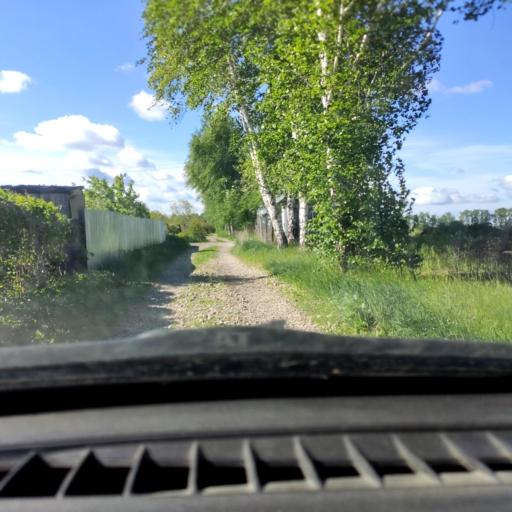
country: RU
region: Samara
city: Tol'yatti
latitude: 53.6279
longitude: 49.4024
